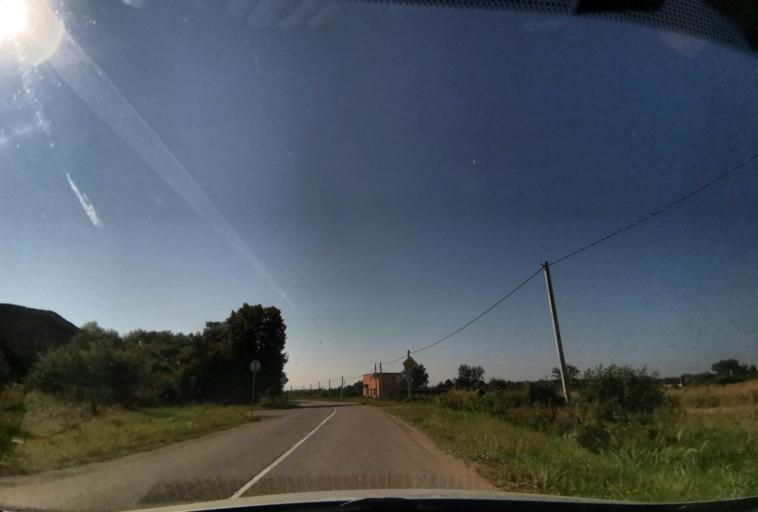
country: RU
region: Kaliningrad
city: Primorsk
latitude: 54.7594
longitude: 20.0115
